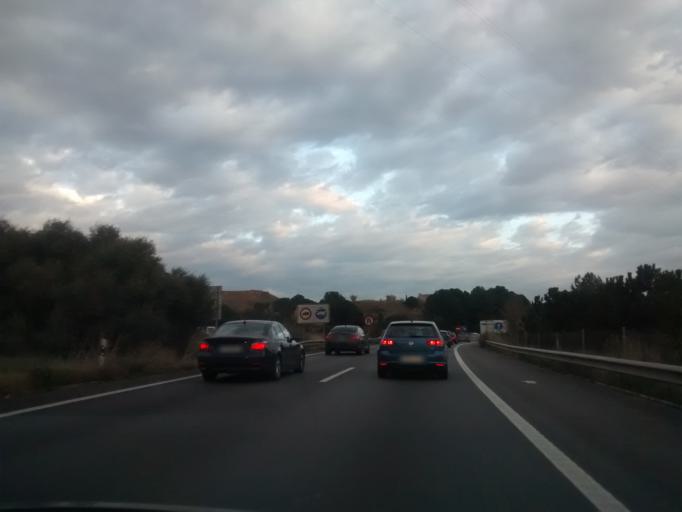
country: ES
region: Catalonia
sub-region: Provincia de Barcelona
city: Palleja
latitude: 41.4464
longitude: 1.9986
